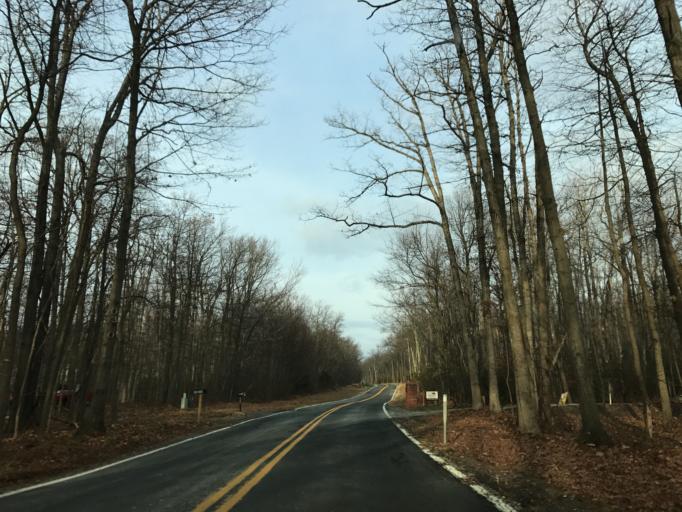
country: US
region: Maryland
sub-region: Frederick County
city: Myersville
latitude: 39.5182
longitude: -77.4986
